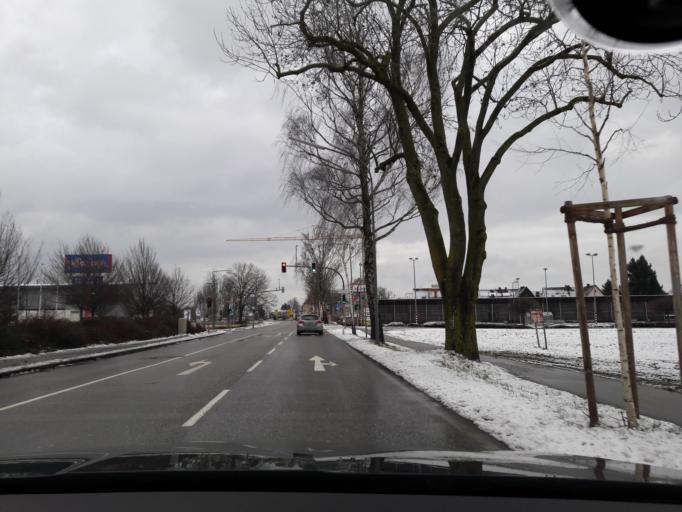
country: DE
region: Bavaria
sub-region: Upper Bavaria
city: Hebertshausen
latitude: 48.2594
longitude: 11.4696
